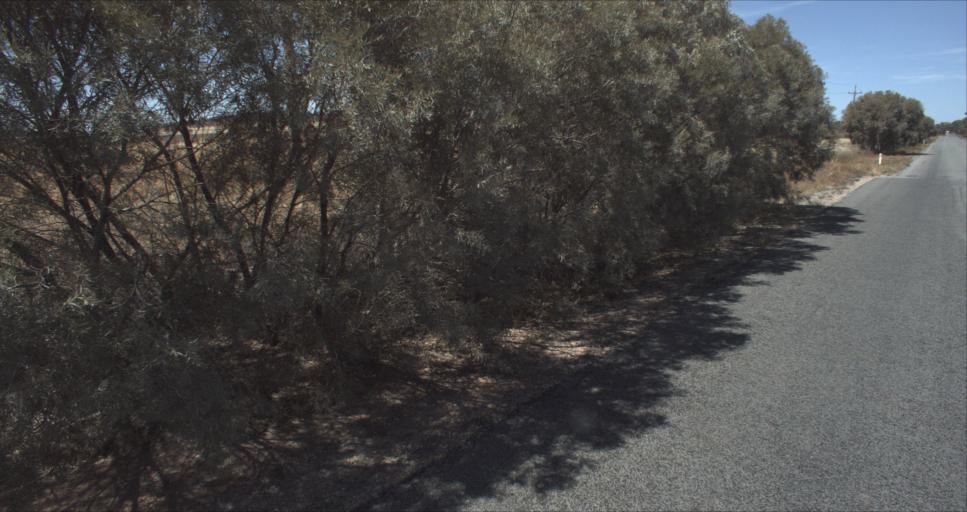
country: AU
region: New South Wales
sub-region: Leeton
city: Leeton
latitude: -34.6361
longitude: 146.4616
